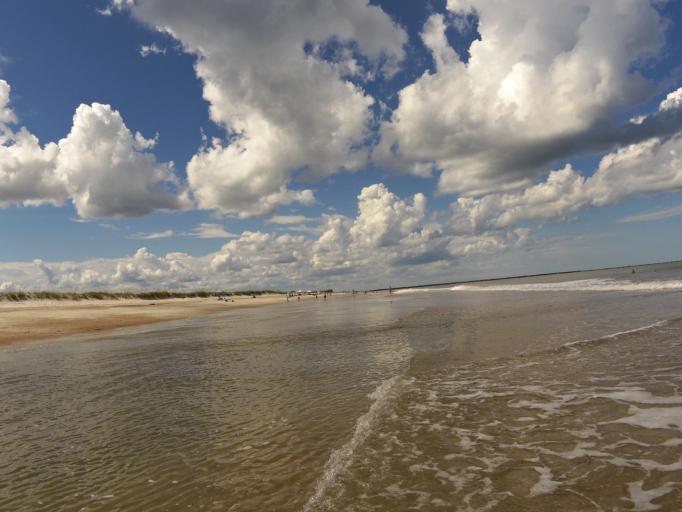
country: US
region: Florida
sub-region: Nassau County
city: Fernandina Beach
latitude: 30.6956
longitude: -81.4271
